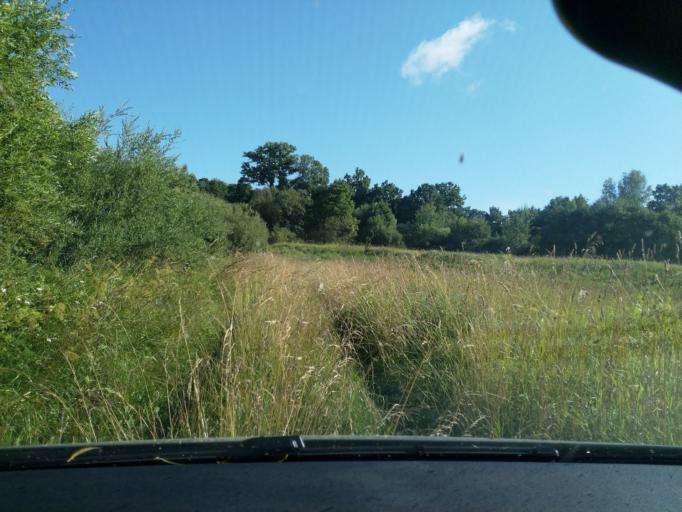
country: LV
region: Kuldigas Rajons
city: Kuldiga
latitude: 56.9787
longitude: 21.9735
